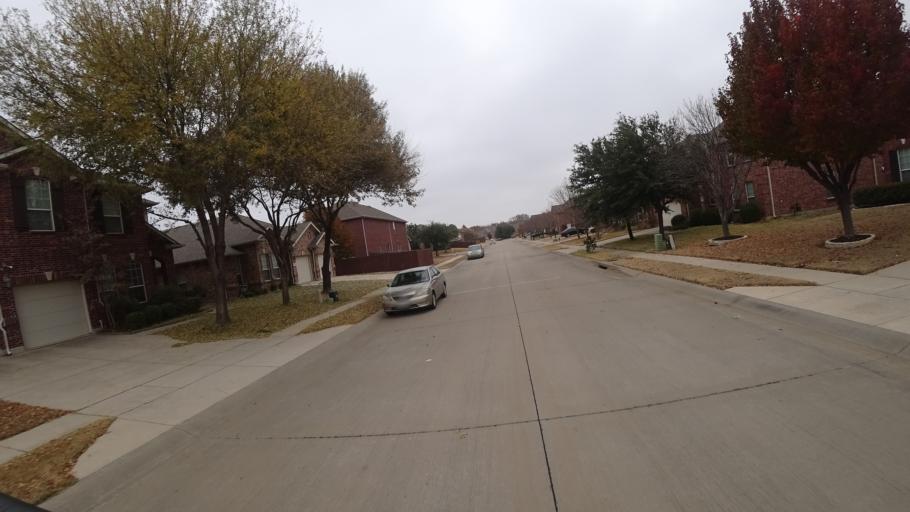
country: US
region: Texas
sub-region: Denton County
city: The Colony
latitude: 33.0662
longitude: -96.9035
